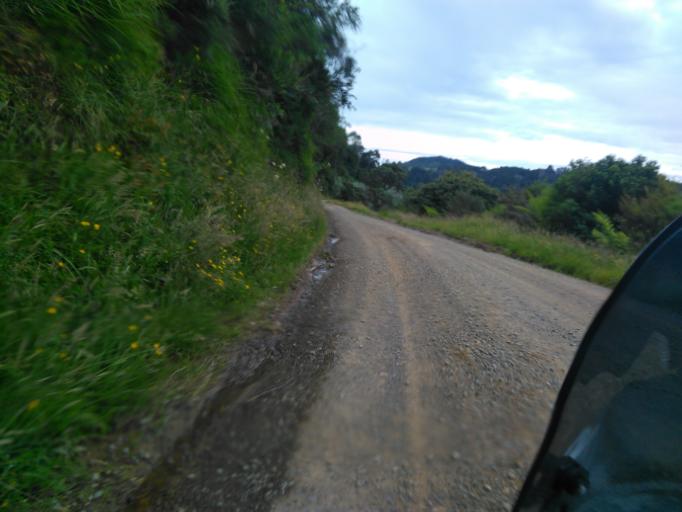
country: NZ
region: Bay of Plenty
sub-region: Opotiki District
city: Opotiki
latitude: -38.0306
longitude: 177.4413
